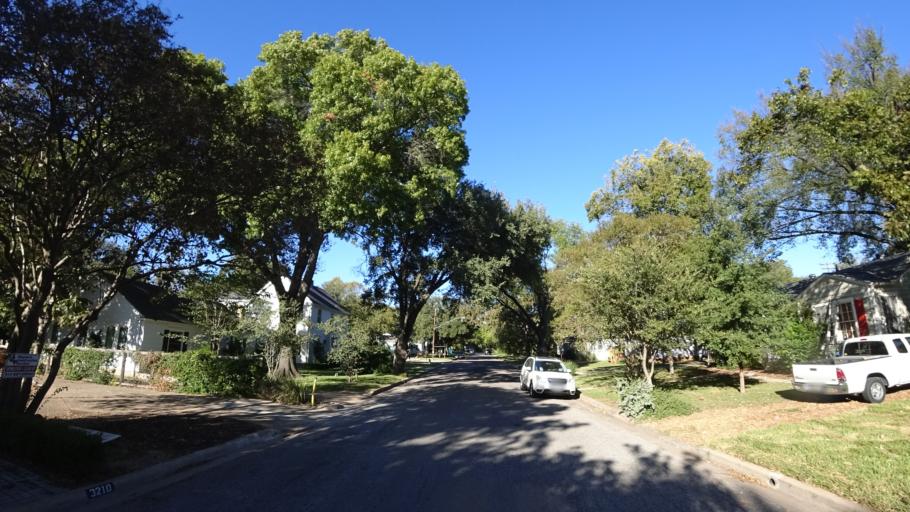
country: US
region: Texas
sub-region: Travis County
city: Austin
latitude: 30.3055
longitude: -97.7550
